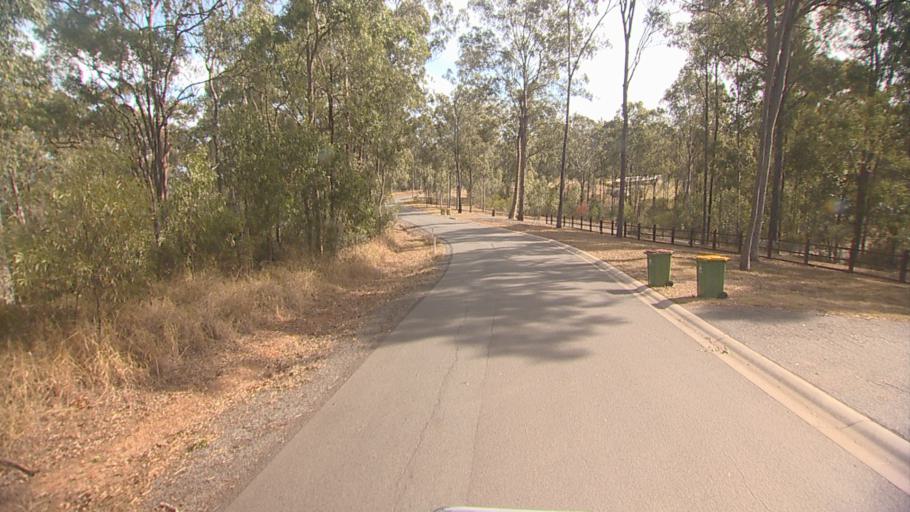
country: AU
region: Queensland
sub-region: Logan
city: Cedar Vale
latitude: -27.8955
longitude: 152.9990
